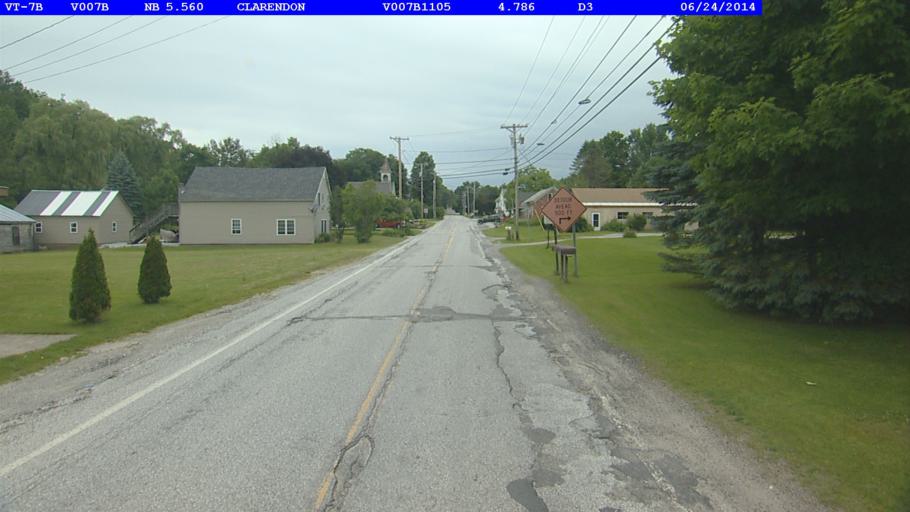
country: US
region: Vermont
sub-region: Rutland County
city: Rutland
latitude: 43.5654
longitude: -72.9659
